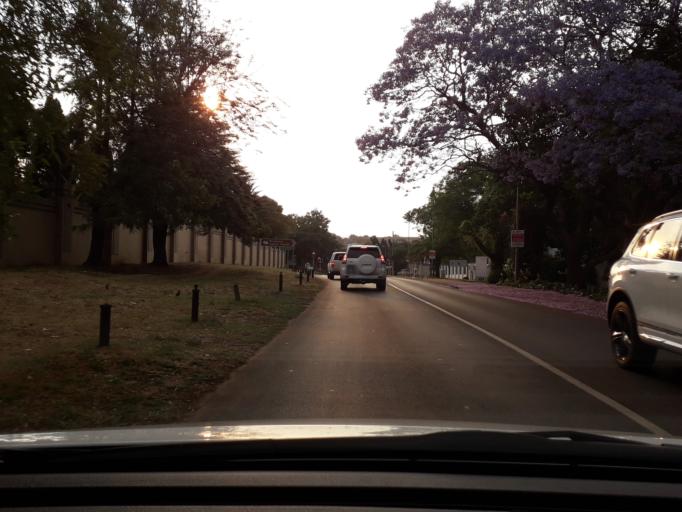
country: ZA
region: Gauteng
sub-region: City of Johannesburg Metropolitan Municipality
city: Midrand
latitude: -26.0477
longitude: 28.0323
